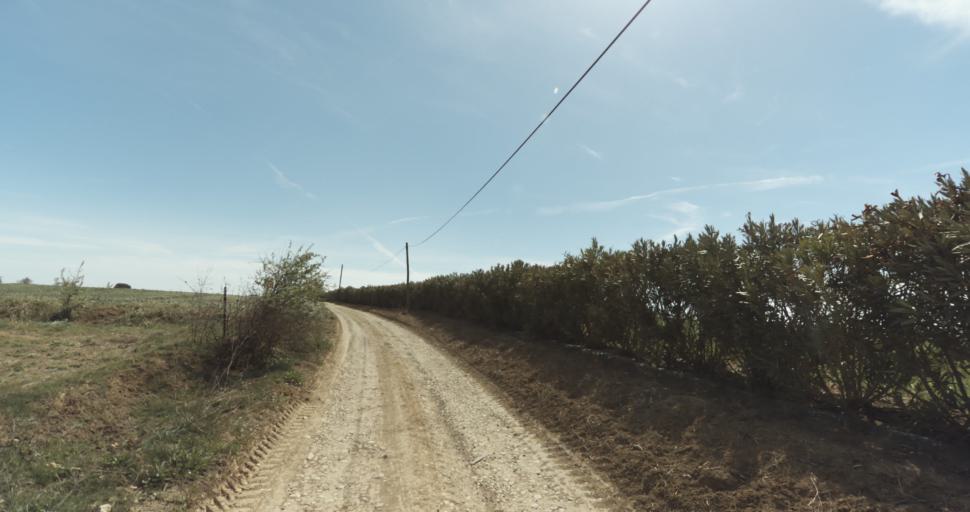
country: FR
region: Languedoc-Roussillon
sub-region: Departement de l'Herault
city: Pinet
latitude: 43.4051
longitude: 3.5514
